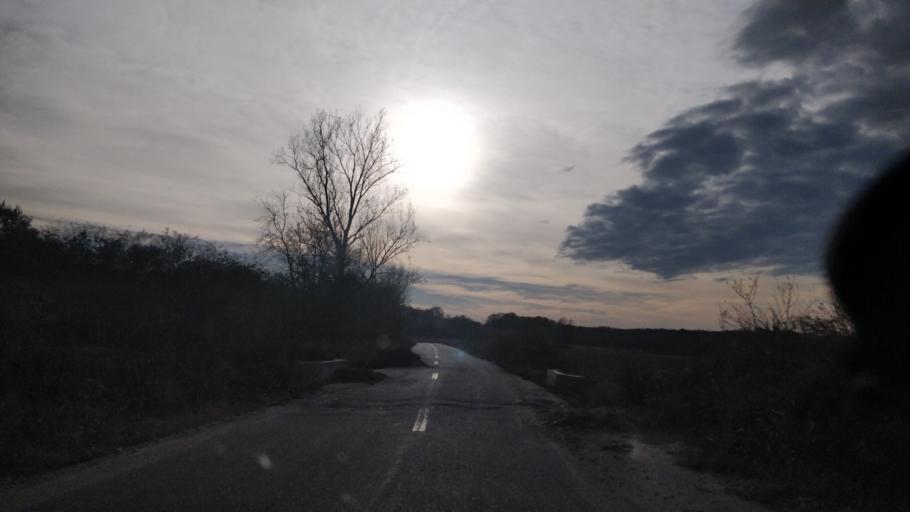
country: RO
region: Giurgiu
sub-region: Comuna Bucsani
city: Bucsani
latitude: 44.3401
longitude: 25.6651
